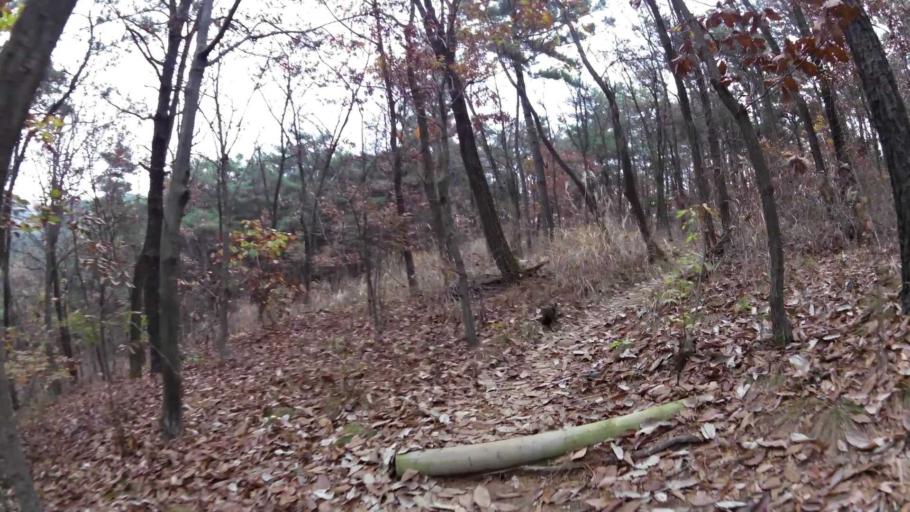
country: KR
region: Daegu
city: Daegu
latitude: 35.8571
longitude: 128.6556
